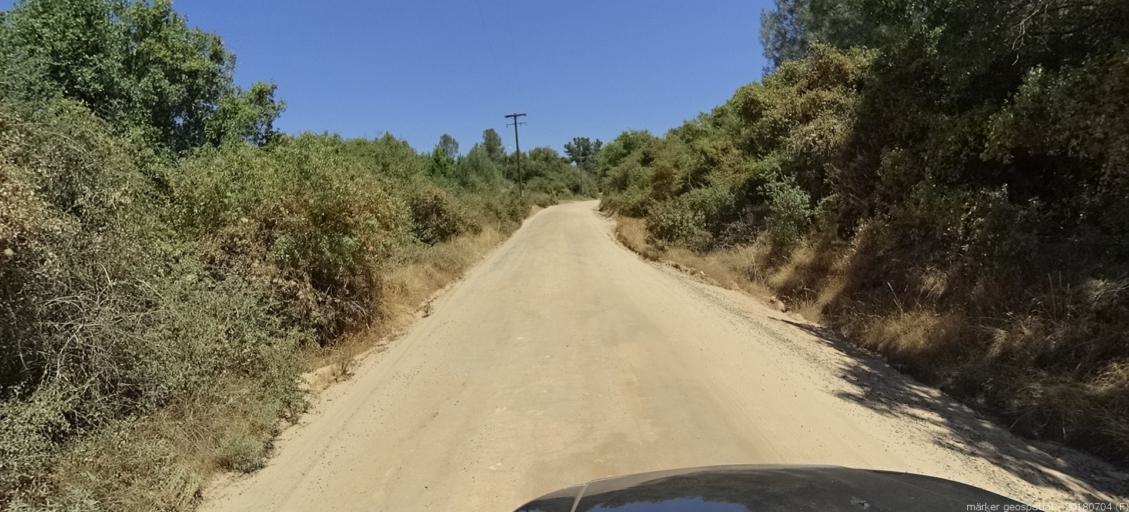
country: US
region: California
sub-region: Fresno County
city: Auberry
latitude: 37.2073
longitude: -119.5423
